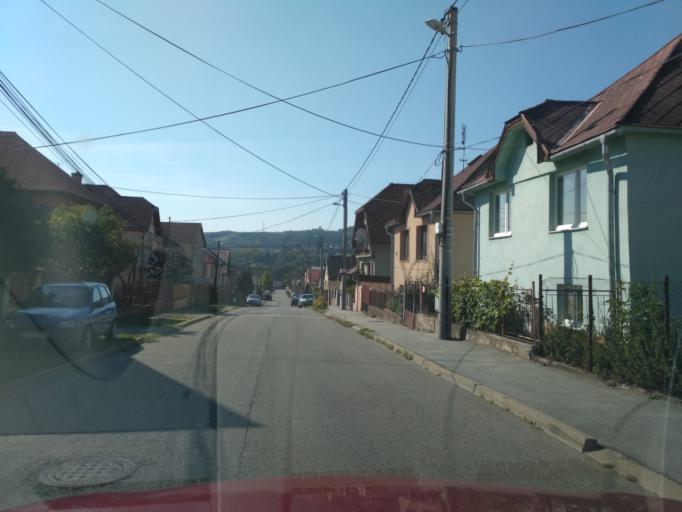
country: SK
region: Kosicky
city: Kosice
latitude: 48.7557
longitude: 21.2605
